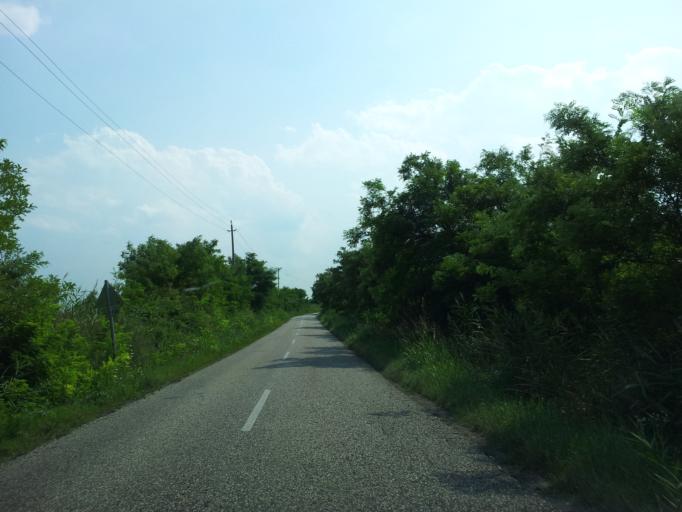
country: HU
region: Pest
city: Szigetujfalu
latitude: 47.2141
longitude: 18.9186
